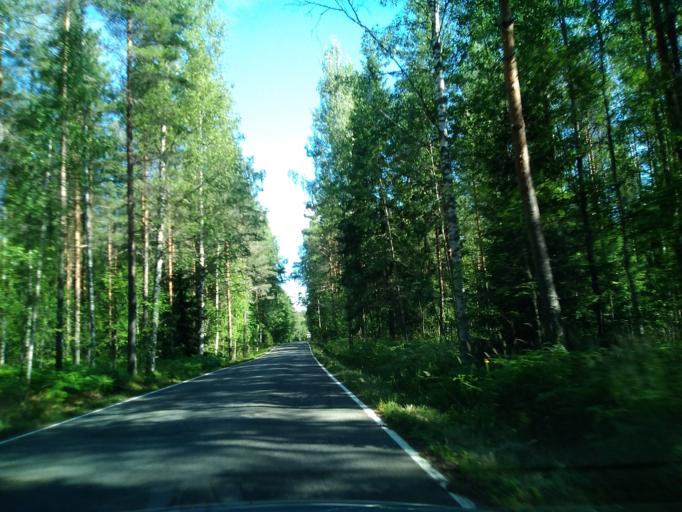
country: FI
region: Haeme
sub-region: Haemeenlinna
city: Renko
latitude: 60.7929
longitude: 24.0845
